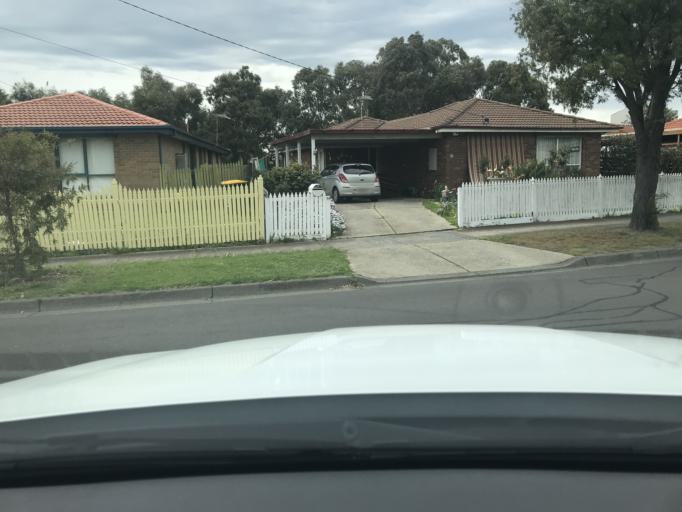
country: AU
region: Victoria
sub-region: Hume
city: Craigieburn
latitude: -37.6075
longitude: 144.9393
